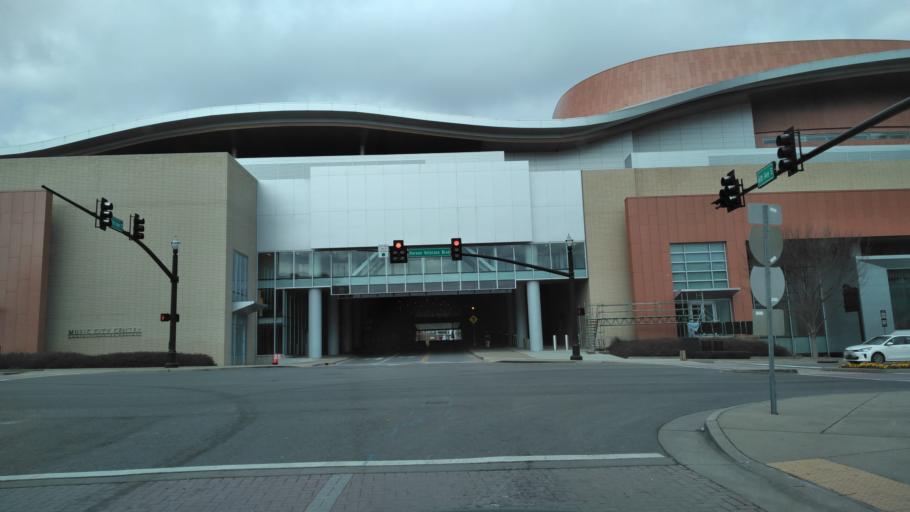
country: US
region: Tennessee
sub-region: Davidson County
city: Nashville
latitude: 36.1557
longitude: -86.7771
